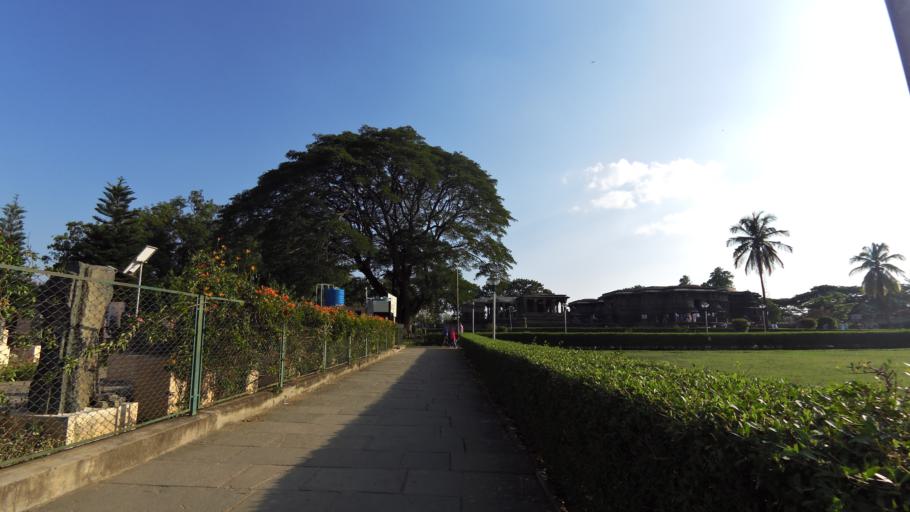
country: IN
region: Karnataka
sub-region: Hassan
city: Belur
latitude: 13.2135
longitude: 75.9945
